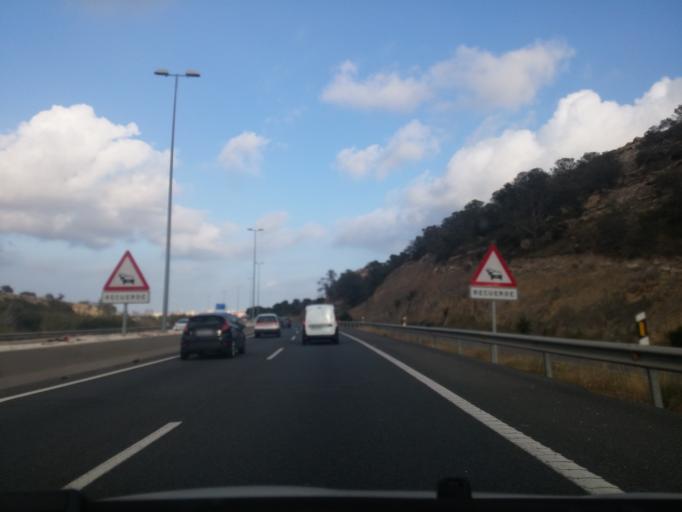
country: ES
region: Valencia
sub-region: Provincia de Alicante
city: Alicante
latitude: 38.3805
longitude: -0.4707
